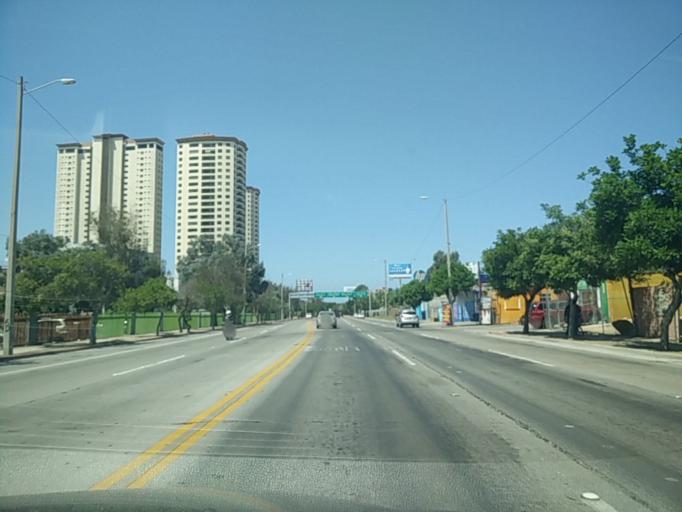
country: MX
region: Baja California
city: Tijuana
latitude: 32.5367
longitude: -117.0189
